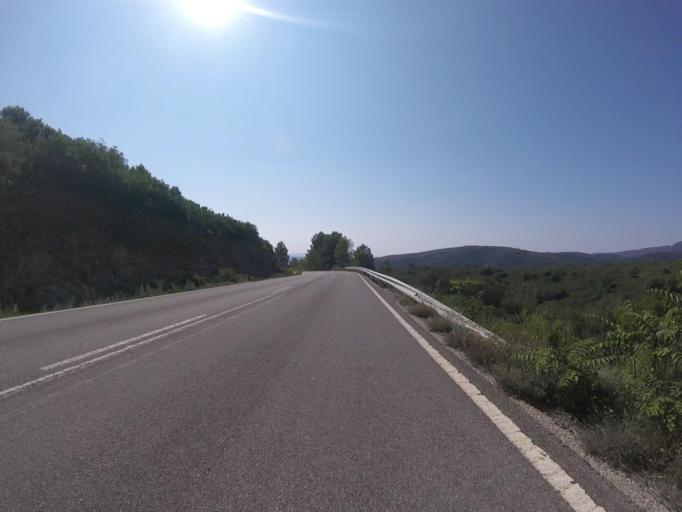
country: ES
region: Valencia
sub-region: Provincia de Castello
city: Benafigos
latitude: 40.2570
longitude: -0.2165
